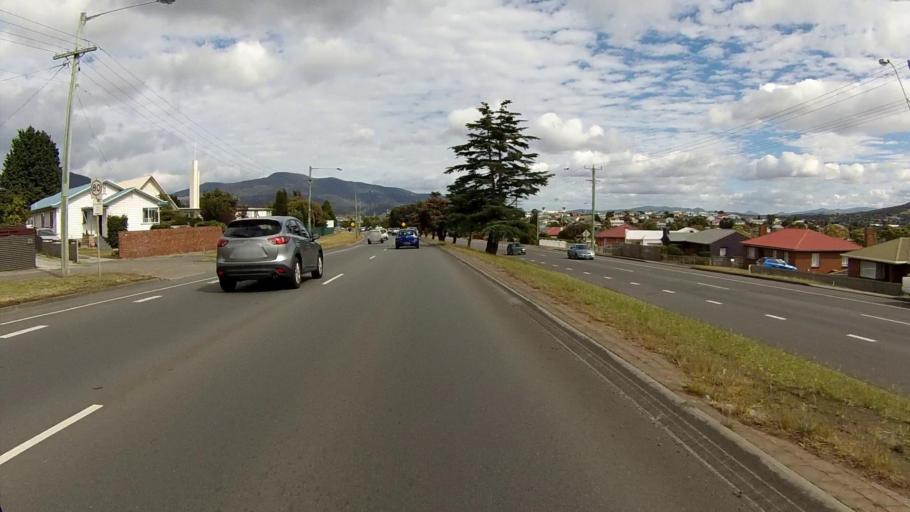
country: AU
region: Tasmania
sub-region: Glenorchy
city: Goodwood
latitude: -42.8327
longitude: 147.2968
